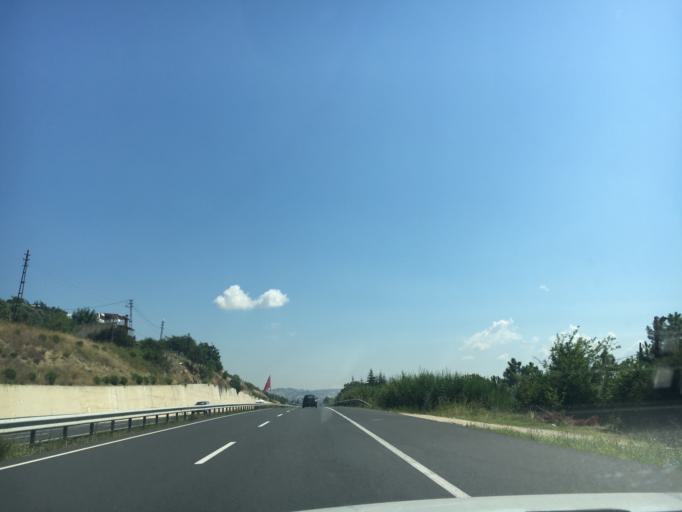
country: TR
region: Tekirdag
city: Sultankoy
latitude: 41.0236
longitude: 27.9965
